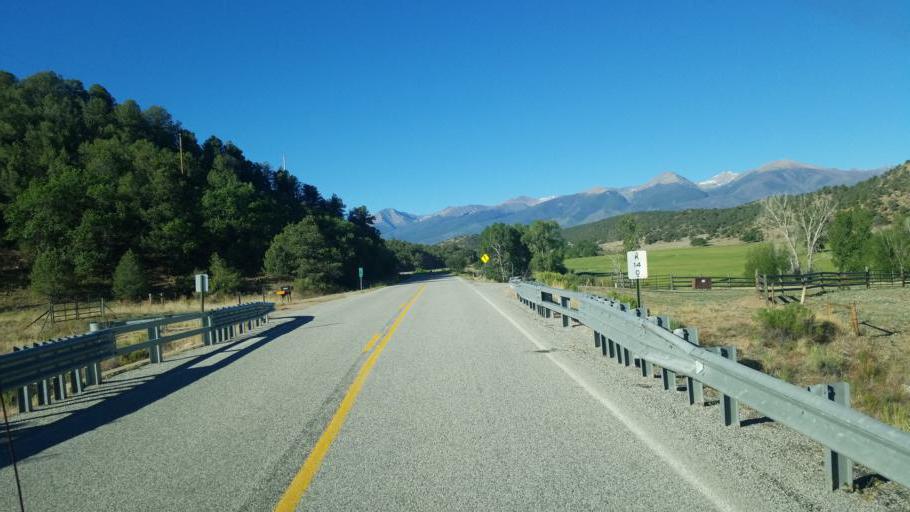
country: US
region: Colorado
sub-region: Custer County
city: Westcliffe
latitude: 38.3589
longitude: -105.5894
